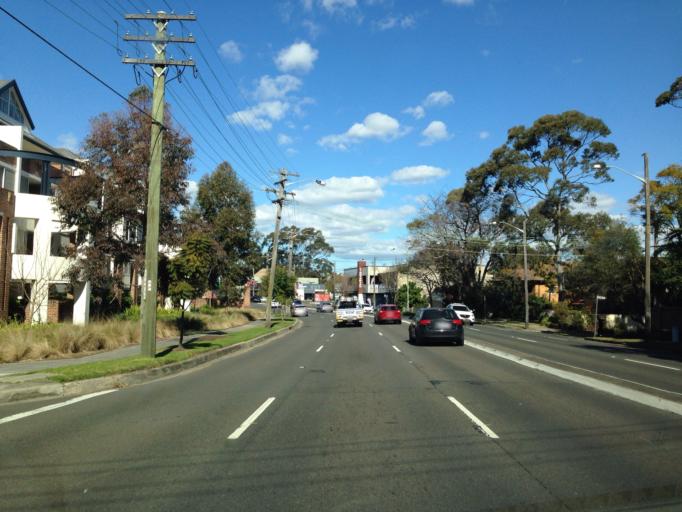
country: AU
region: New South Wales
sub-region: Ku-ring-gai
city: Killara
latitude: -33.7618
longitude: 151.1551
